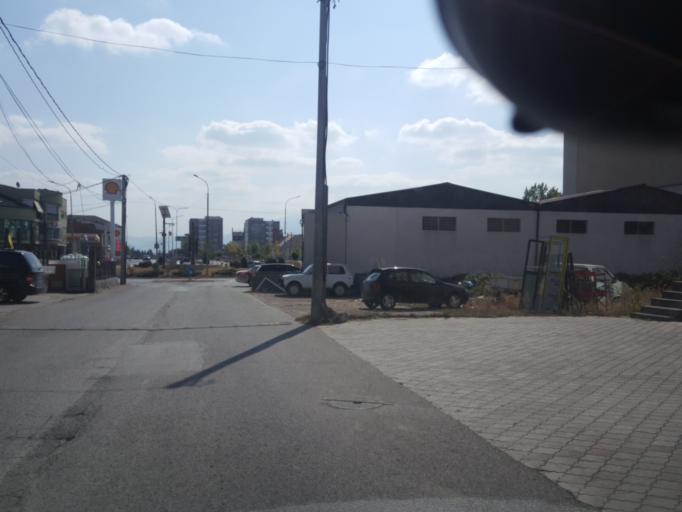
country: XK
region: Gjakova
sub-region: Komuna e Gjakoves
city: Gjakove
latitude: 42.3885
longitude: 20.4343
